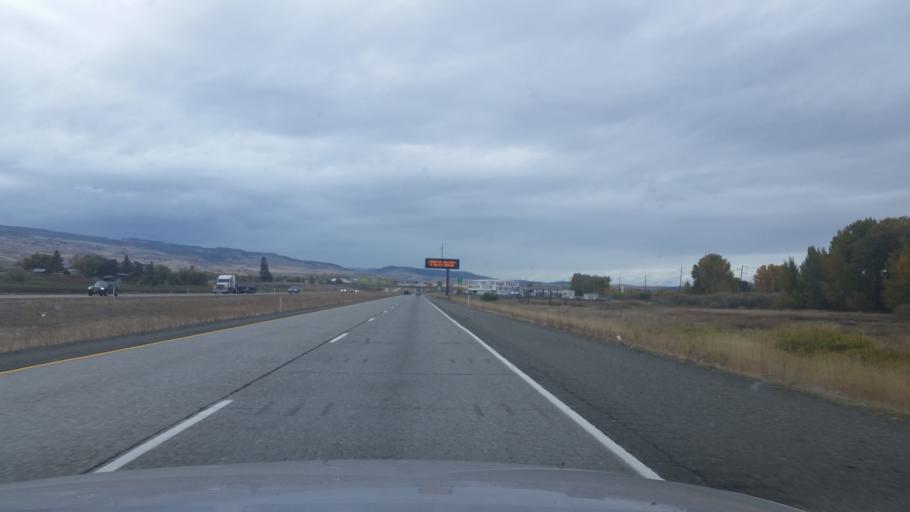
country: US
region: Washington
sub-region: Kittitas County
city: Ellensburg
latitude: 47.0512
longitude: -120.6566
